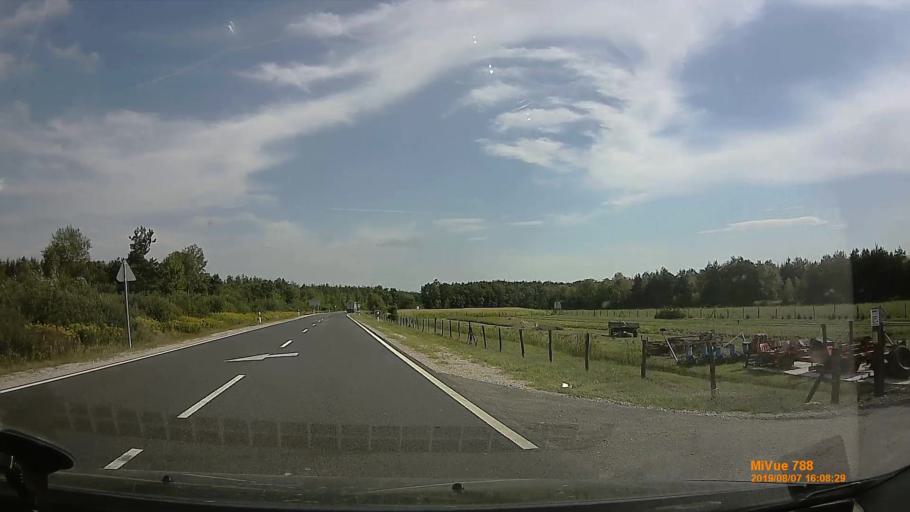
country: HU
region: Zala
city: Zalalovo
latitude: 46.9076
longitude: 16.6028
